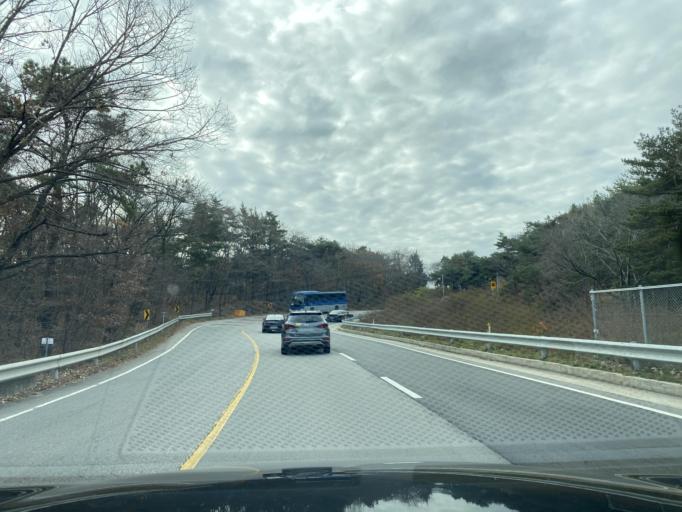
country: KR
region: Chungcheongnam-do
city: Hongsung
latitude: 36.6665
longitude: 126.6367
